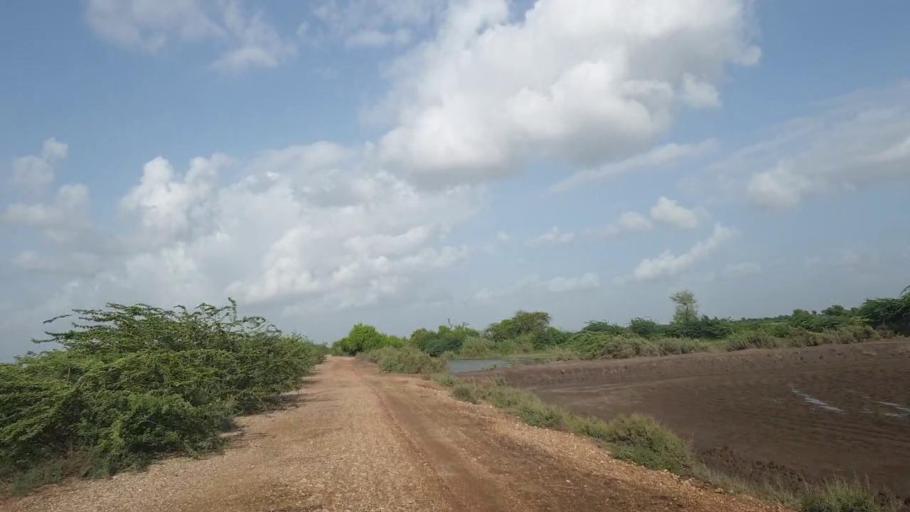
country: PK
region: Sindh
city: Kadhan
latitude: 24.6337
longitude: 69.0931
